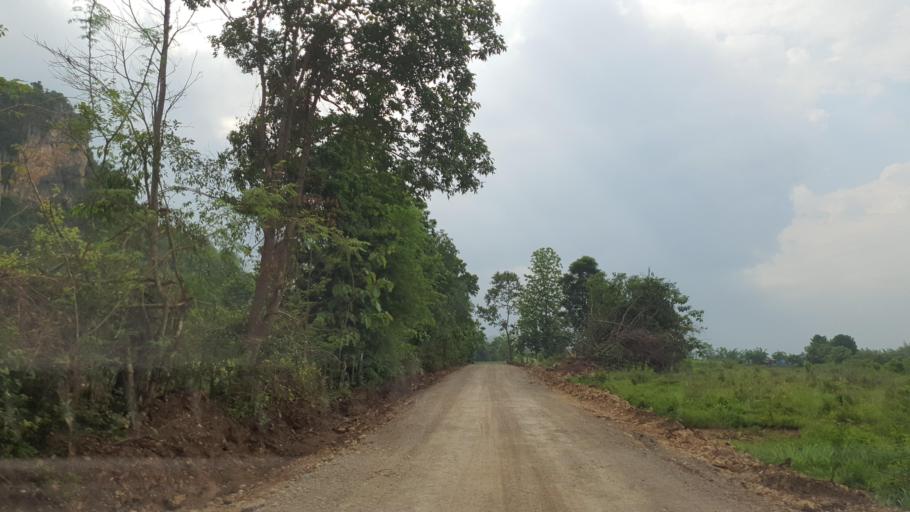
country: TH
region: Sukhothai
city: Thung Saliam
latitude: 17.2573
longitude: 99.5405
